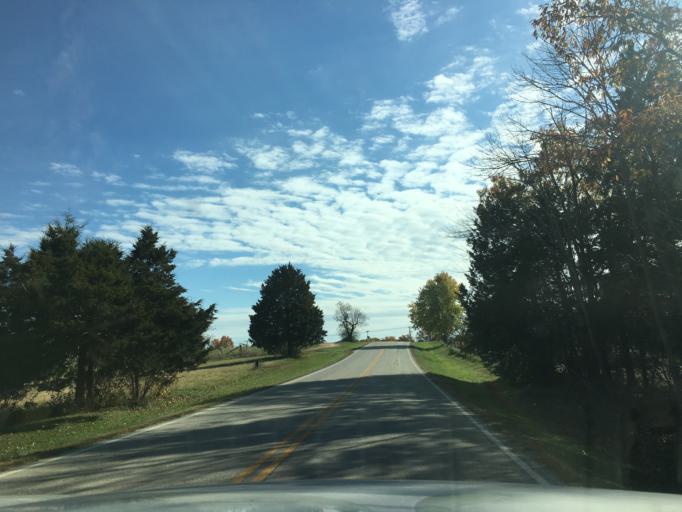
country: US
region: Missouri
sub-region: Osage County
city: Linn
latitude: 38.4270
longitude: -91.8256
